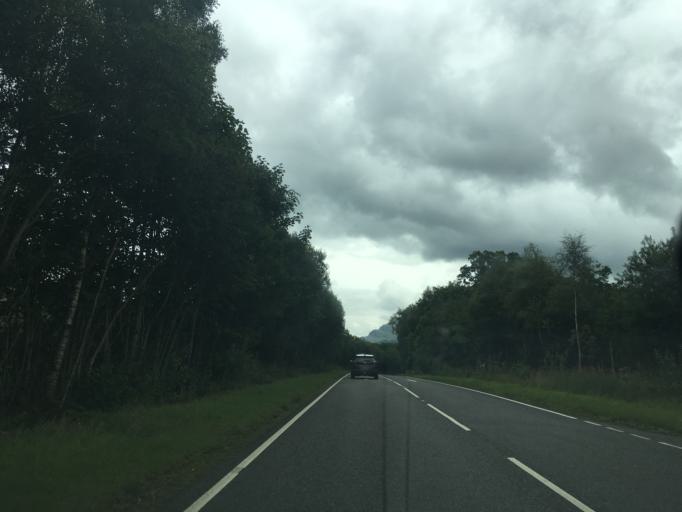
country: GB
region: Scotland
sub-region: Argyll and Bute
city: Garelochhead
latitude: 56.4022
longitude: -4.9885
